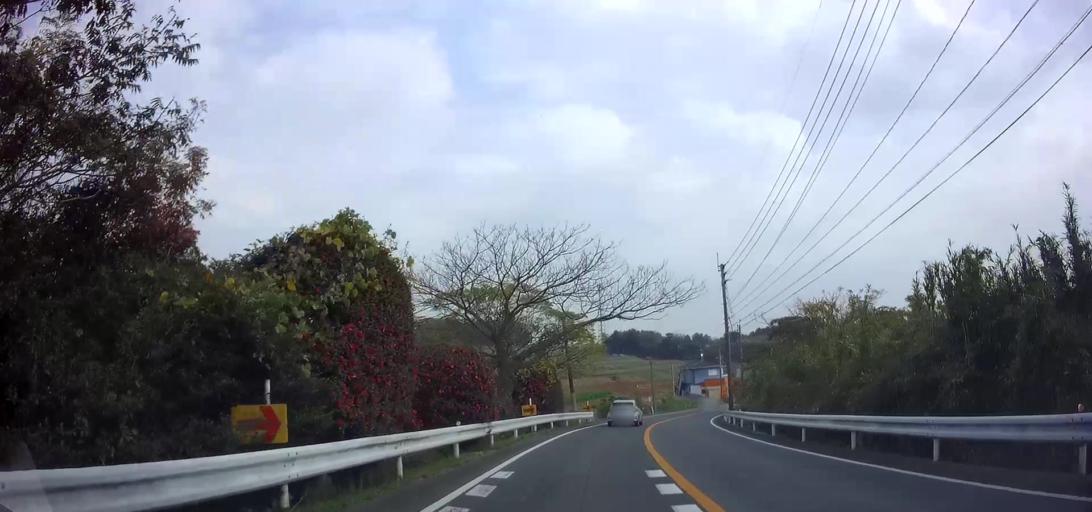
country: JP
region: Nagasaki
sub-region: Isahaya-shi
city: Isahaya
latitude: 32.7894
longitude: 130.0467
